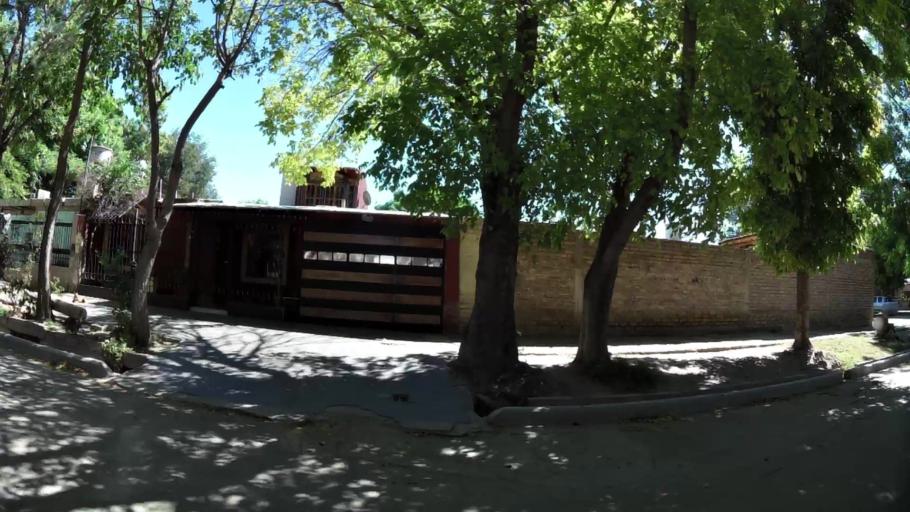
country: AR
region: Mendoza
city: Las Heras
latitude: -32.8321
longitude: -68.8361
